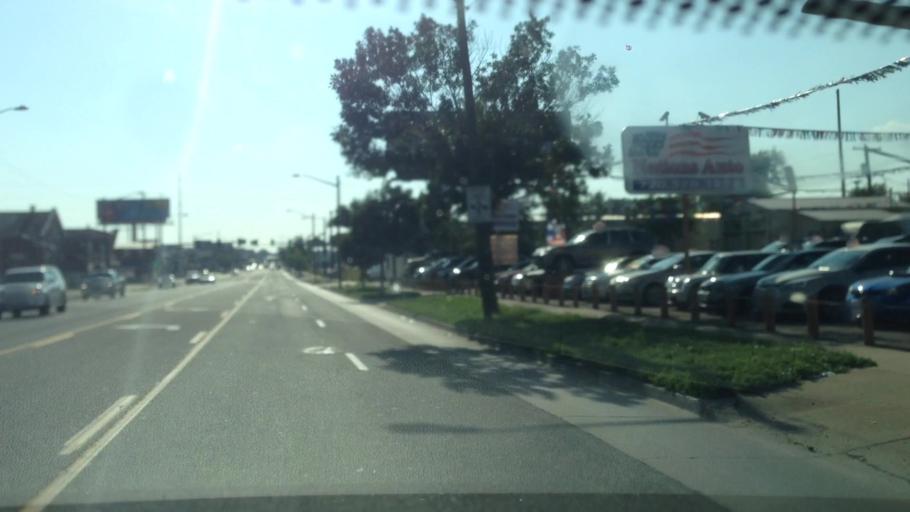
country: US
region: Colorado
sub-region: Denver County
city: Denver
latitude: 39.7112
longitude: -105.0083
